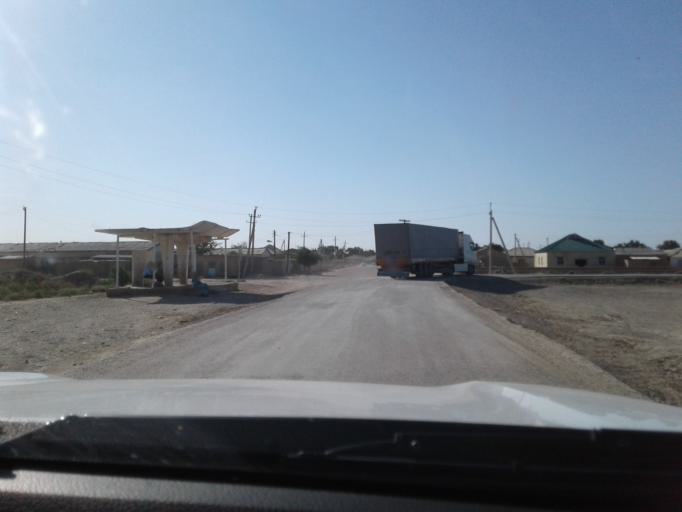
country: IR
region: Razavi Khorasan
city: Kalat-e Naderi
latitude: 37.1942
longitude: 60.0337
